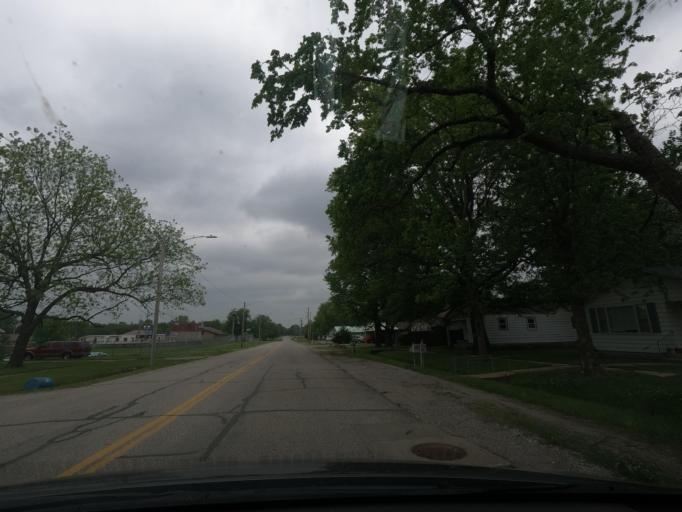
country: US
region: Kansas
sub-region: Cherokee County
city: Columbus
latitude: 37.1755
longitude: -94.8425
